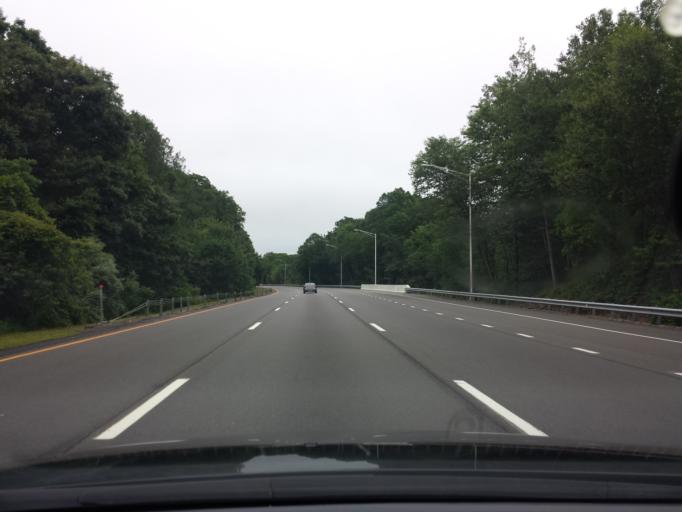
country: US
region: Connecticut
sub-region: New London County
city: Poquonock Bridge
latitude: 41.3623
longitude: -72.0197
